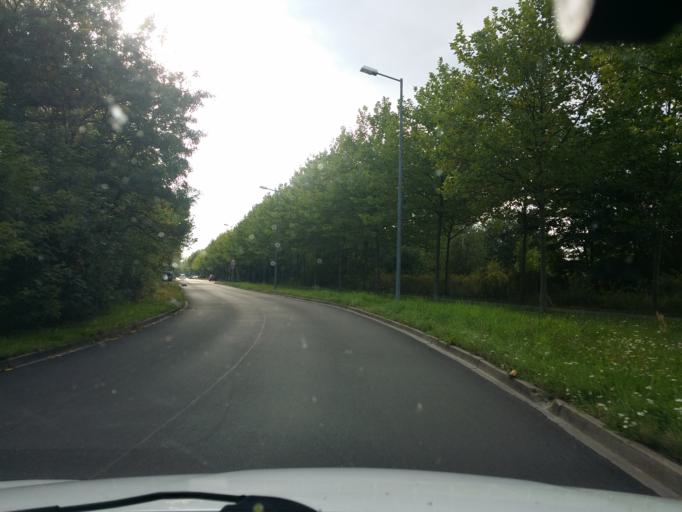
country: DE
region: Saxony
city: Markranstadt
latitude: 51.3267
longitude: 12.2710
